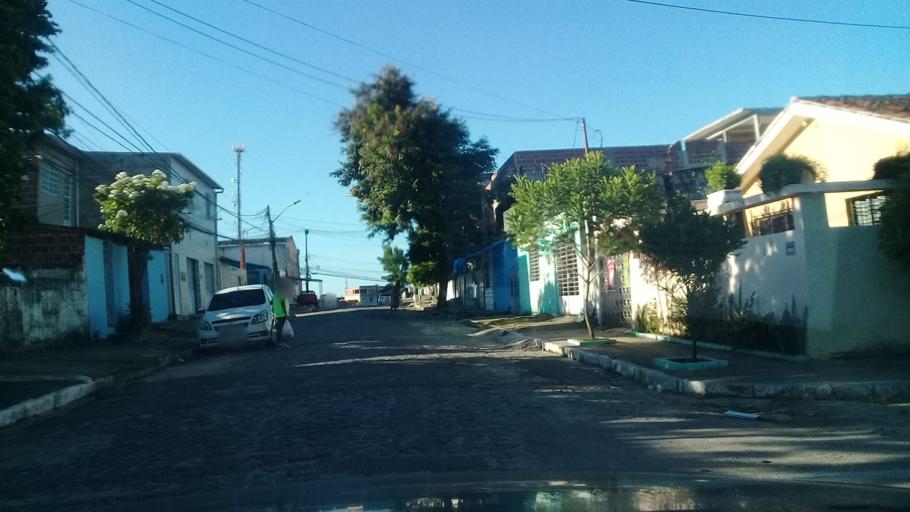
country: BR
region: Pernambuco
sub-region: Jaboatao Dos Guararapes
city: Jaboatao dos Guararapes
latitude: -8.1215
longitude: -34.9551
